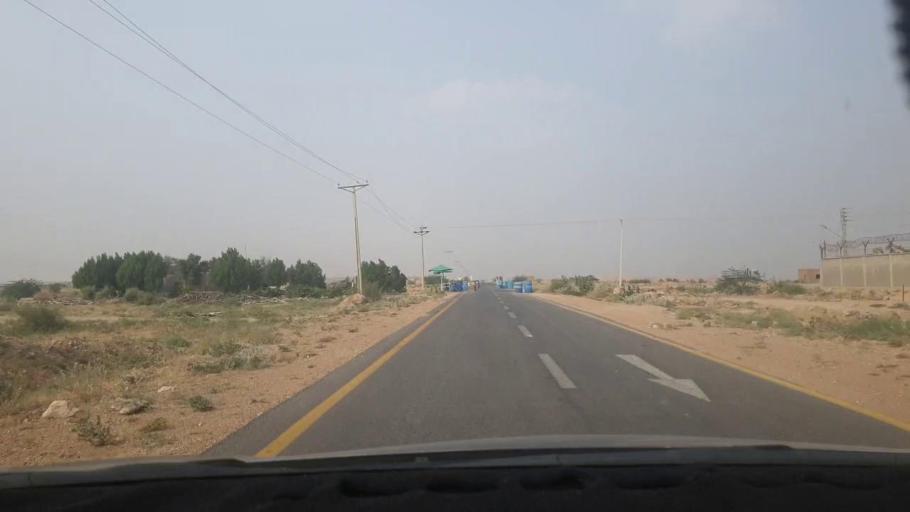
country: PK
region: Sindh
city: Jamshoro
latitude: 25.5644
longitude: 68.3173
